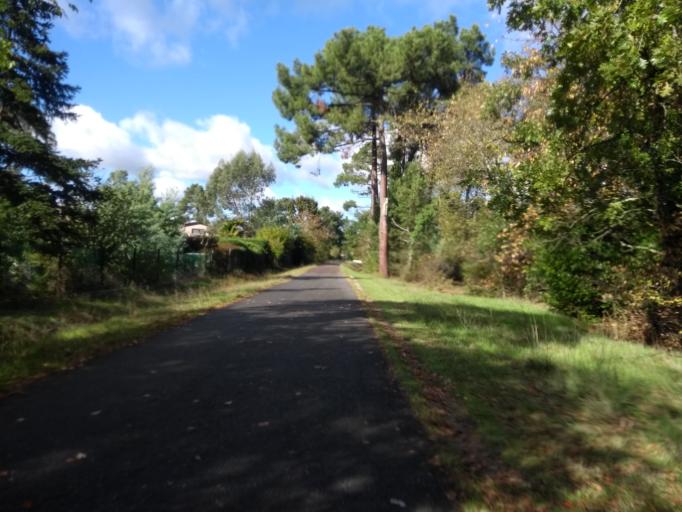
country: FR
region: Aquitaine
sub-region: Departement de la Gironde
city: Saint-Aubin-de-Medoc
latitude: 44.7857
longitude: -0.6984
